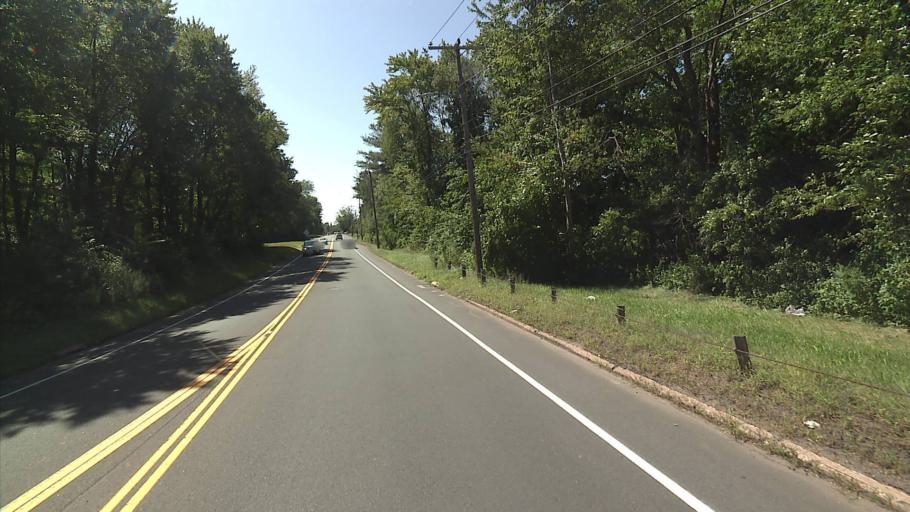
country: US
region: Connecticut
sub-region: Hartford County
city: Blue Hills
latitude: 41.8161
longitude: -72.7482
